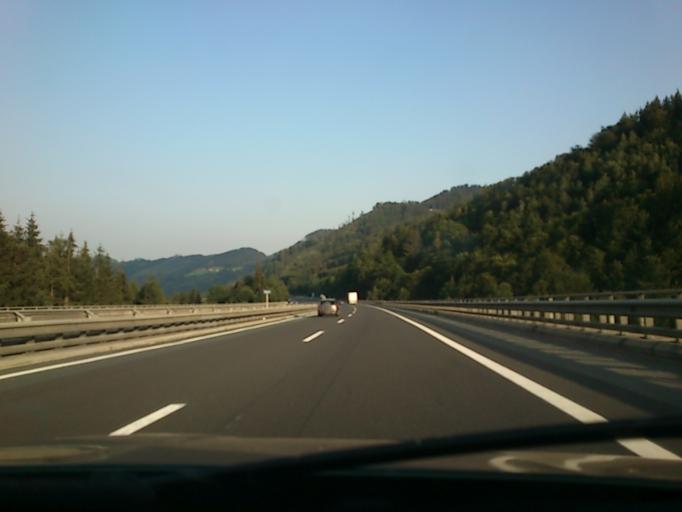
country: AT
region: Styria
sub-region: Politischer Bezirk Graz-Umgebung
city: Ubelbach
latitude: 47.2313
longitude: 15.2148
